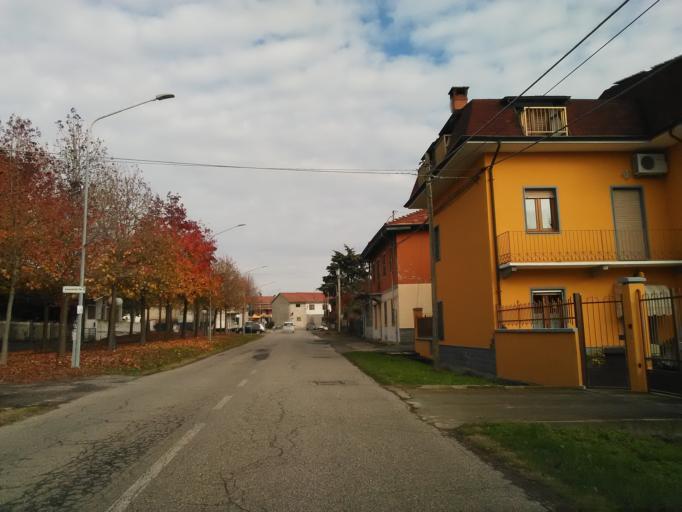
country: IT
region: Piedmont
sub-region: Provincia di Vercelli
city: Alice Castello
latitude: 45.3640
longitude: 8.0706
